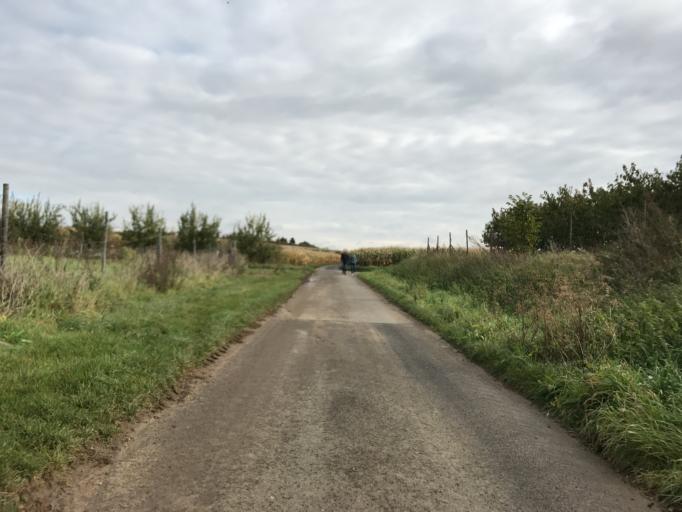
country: DE
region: Rheinland-Pfalz
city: Nieder-Ingelheim
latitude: 49.9651
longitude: 8.0765
